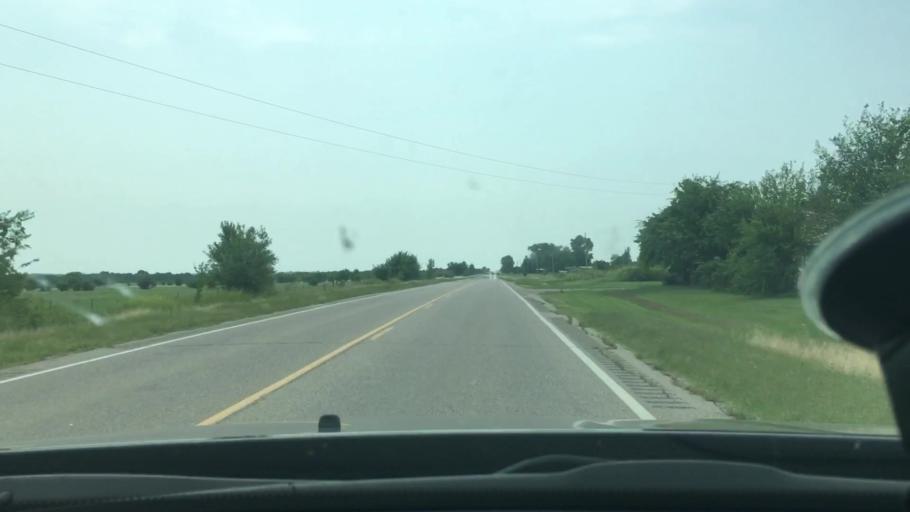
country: US
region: Oklahoma
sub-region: Marshall County
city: Madill
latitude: 34.0531
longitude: -96.7611
